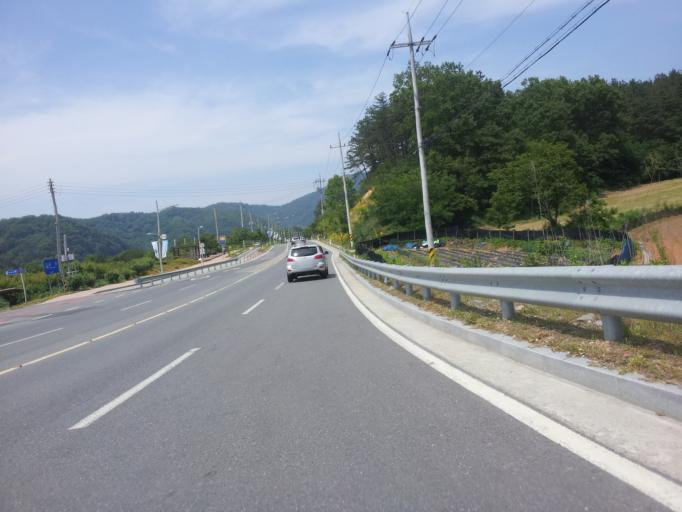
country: KR
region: Daejeon
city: Sintansin
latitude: 36.4592
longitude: 127.4656
